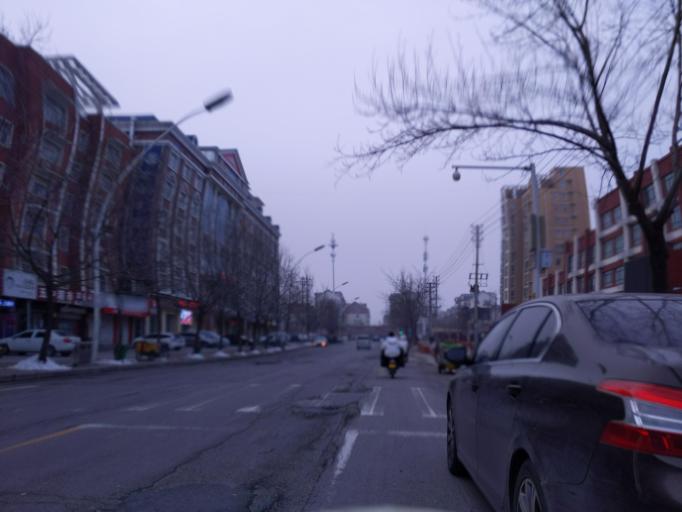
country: CN
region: Henan Sheng
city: Zhongyuanlu
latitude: 35.7652
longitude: 115.0492
